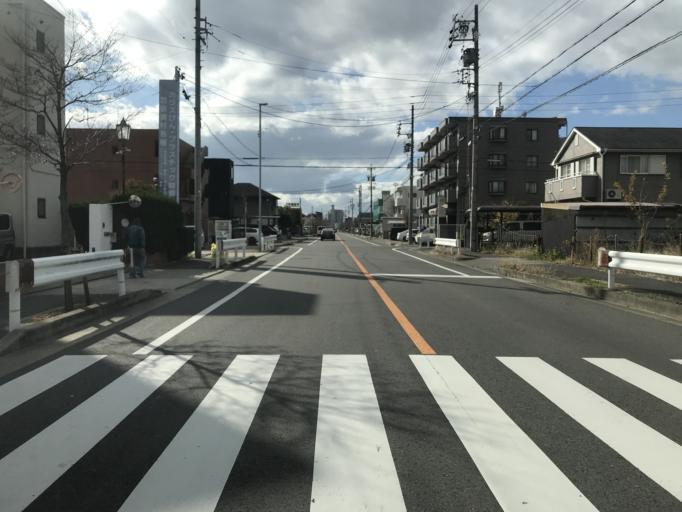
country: JP
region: Aichi
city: Nagoya-shi
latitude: 35.1833
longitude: 136.8571
